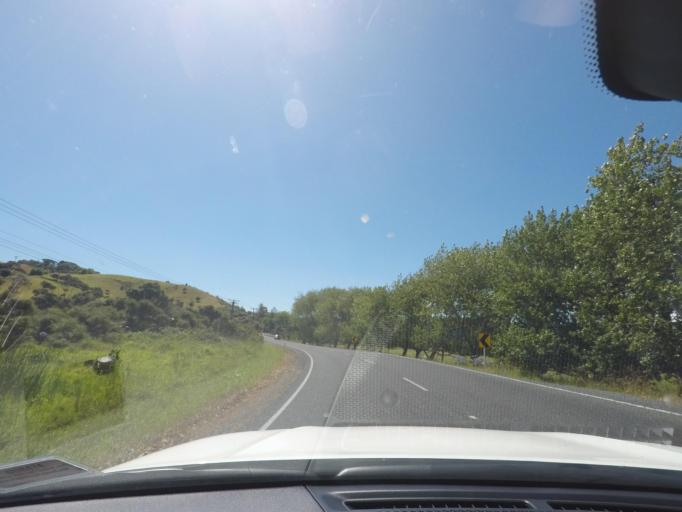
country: NZ
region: Auckland
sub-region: Auckland
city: Parakai
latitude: -36.5891
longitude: 174.3389
